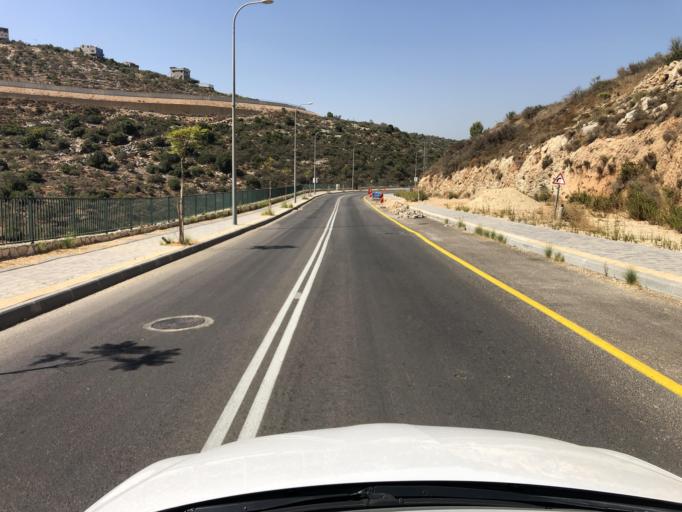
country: PS
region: West Bank
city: An Nabi Ilyas
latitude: 32.1652
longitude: 35.0150
